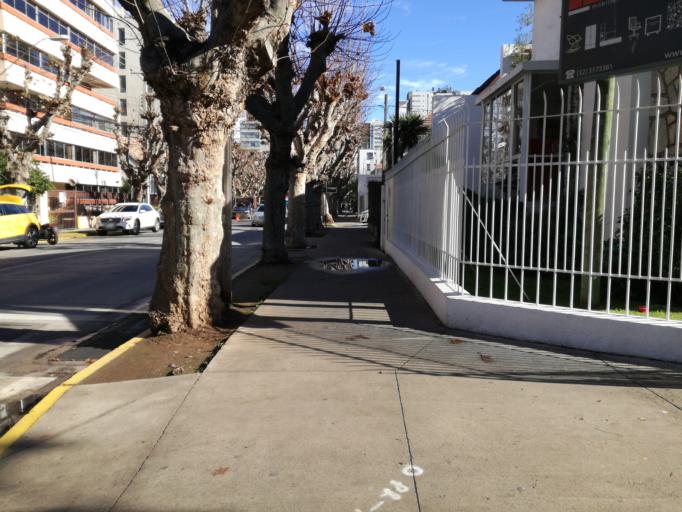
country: CL
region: Valparaiso
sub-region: Provincia de Valparaiso
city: Vina del Mar
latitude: -33.0209
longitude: -71.5550
